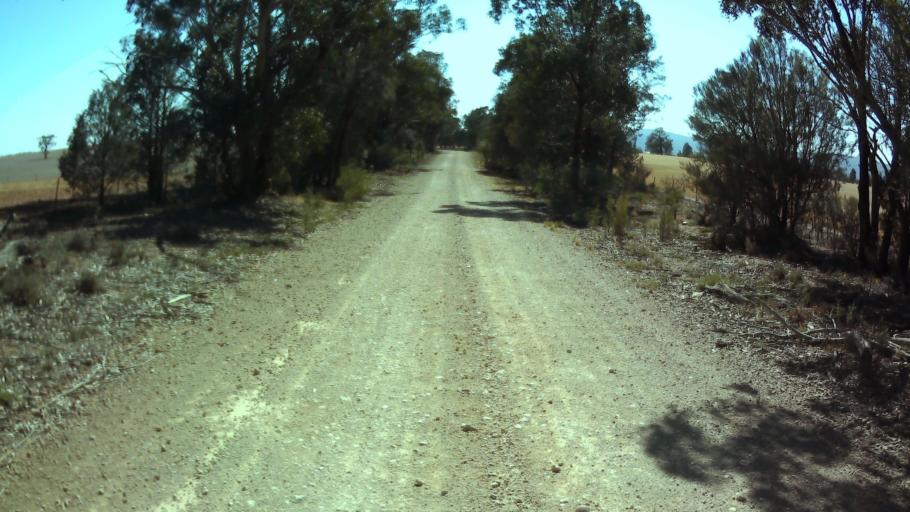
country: AU
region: New South Wales
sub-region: Weddin
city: Grenfell
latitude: -33.9038
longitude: 147.8609
